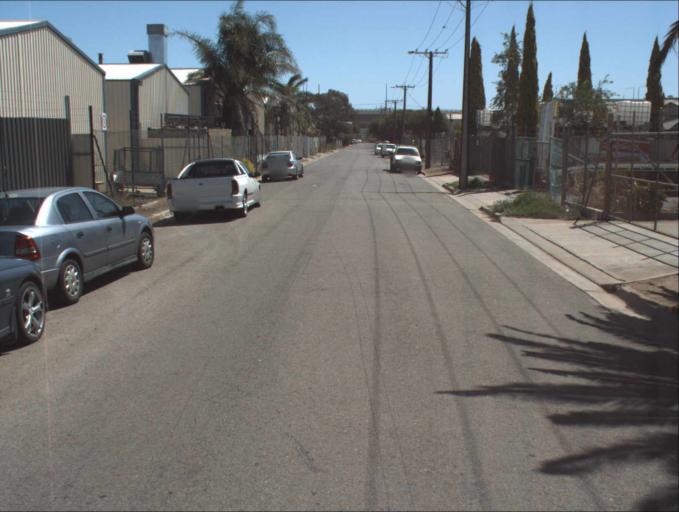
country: AU
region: South Australia
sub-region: Port Adelaide Enfield
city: Blair Athol
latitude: -34.8381
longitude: 138.5677
